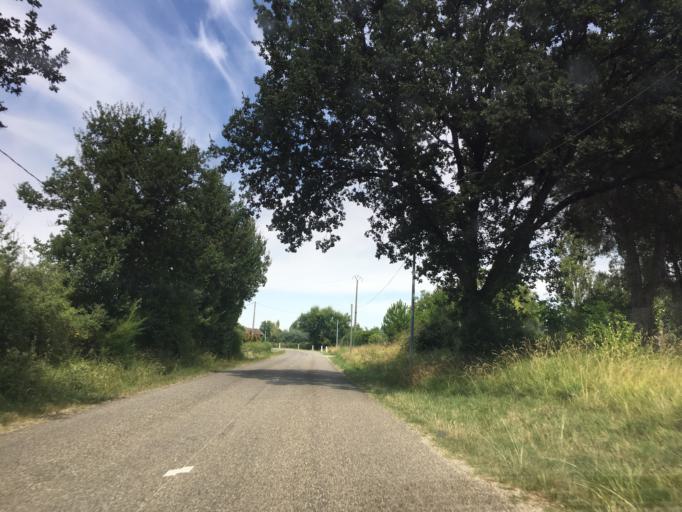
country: FR
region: Midi-Pyrenees
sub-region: Departement du Gers
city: Fleurance
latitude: 43.8239
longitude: 0.6394
